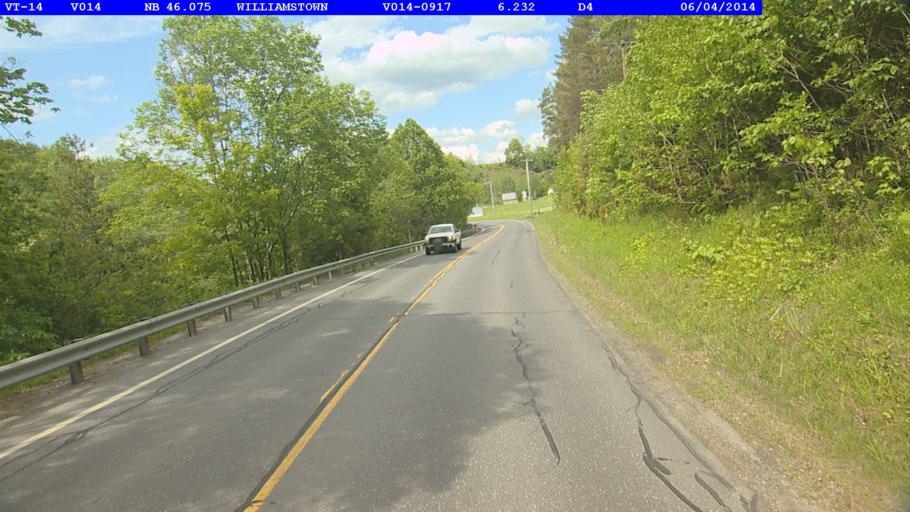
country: US
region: Vermont
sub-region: Orange County
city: Williamstown
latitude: 44.1440
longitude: -72.5257
